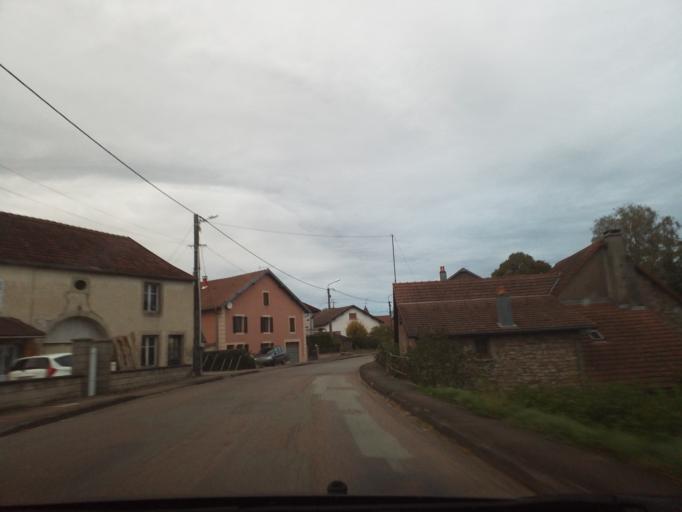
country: FR
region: Franche-Comte
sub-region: Departement de la Haute-Saone
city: Saint-Germain
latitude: 47.7203
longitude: 6.5272
